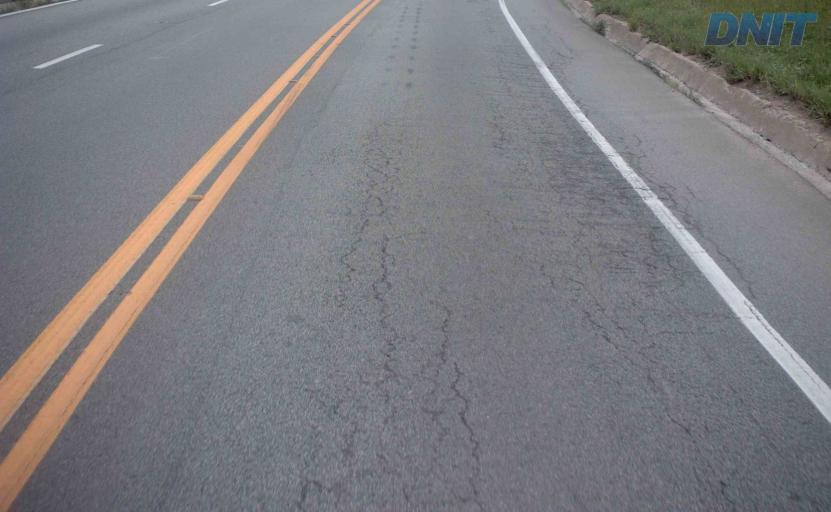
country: BR
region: Minas Gerais
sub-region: Nova Era
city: Nova Era
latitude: -19.6452
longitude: -42.9114
